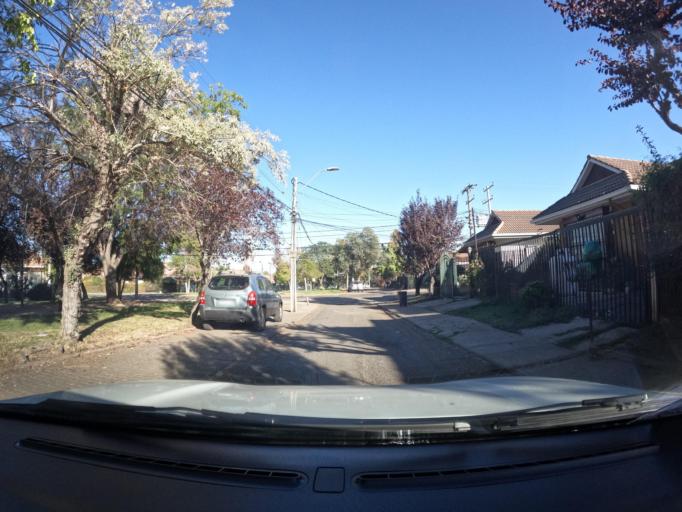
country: CL
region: Santiago Metropolitan
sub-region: Provincia de Santiago
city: Villa Presidente Frei, Nunoa, Santiago, Chile
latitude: -33.4784
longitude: -70.5528
